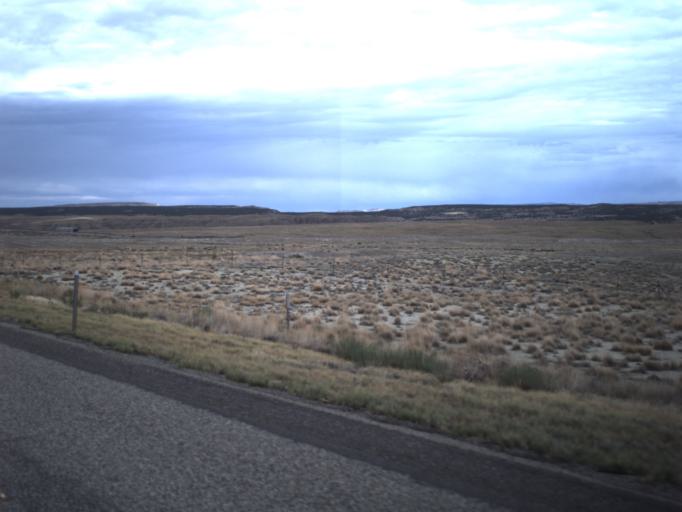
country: US
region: Colorado
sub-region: Mesa County
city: Loma
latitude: 39.1094
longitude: -109.1893
